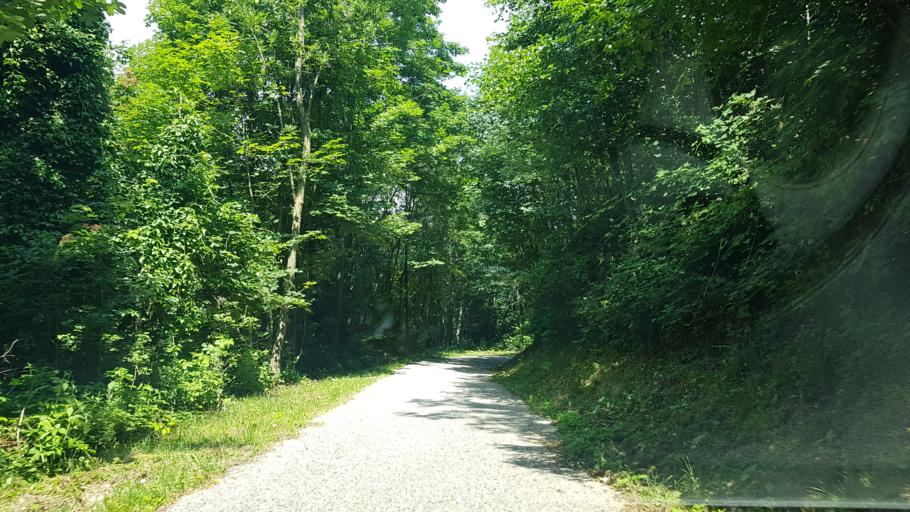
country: IT
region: Friuli Venezia Giulia
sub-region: Provincia di Udine
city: Lusevera
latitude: 46.2426
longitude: 13.2689
